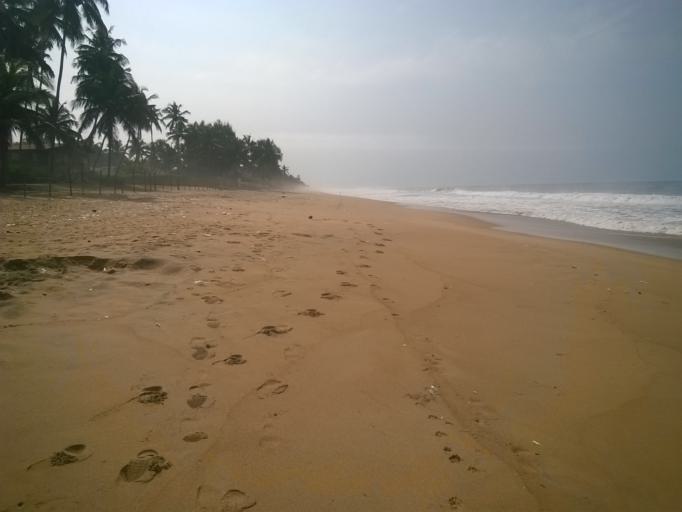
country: CI
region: Sud-Comoe
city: Grand-Bassam
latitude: 5.1957
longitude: -3.7453
